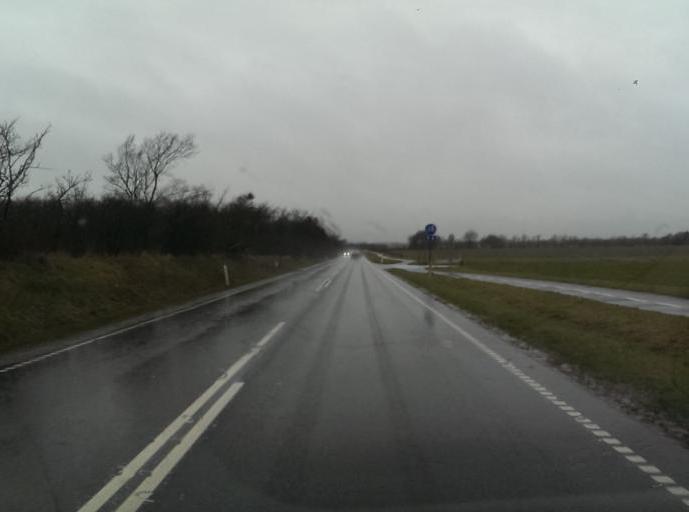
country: DK
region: South Denmark
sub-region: Varde Kommune
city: Olgod
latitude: 55.7279
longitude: 8.6138
